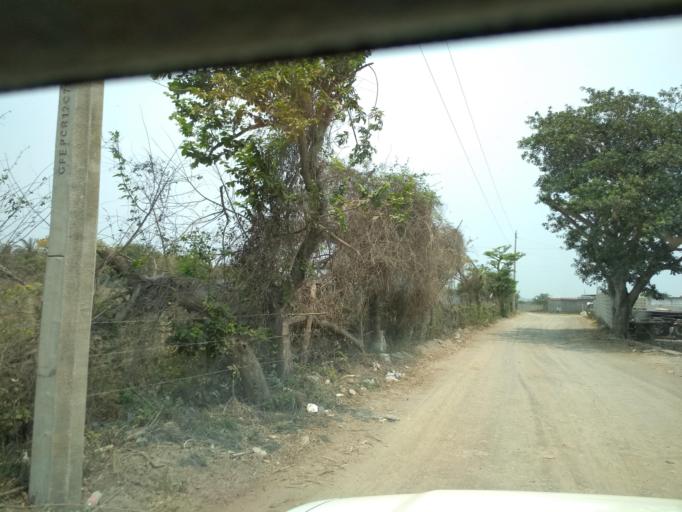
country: MX
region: Veracruz
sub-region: Veracruz
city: Delfino Victoria (Santa Fe)
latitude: 19.2248
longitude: -96.2613
